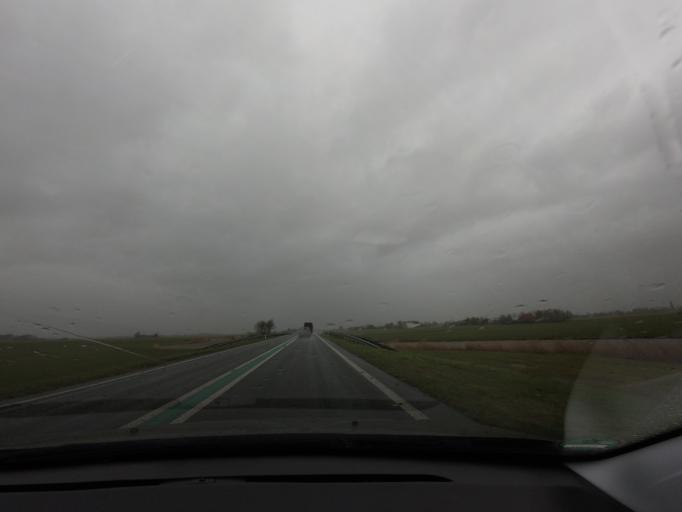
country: NL
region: Friesland
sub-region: Sudwest Fryslan
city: Bolsward
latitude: 53.0871
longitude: 5.5261
